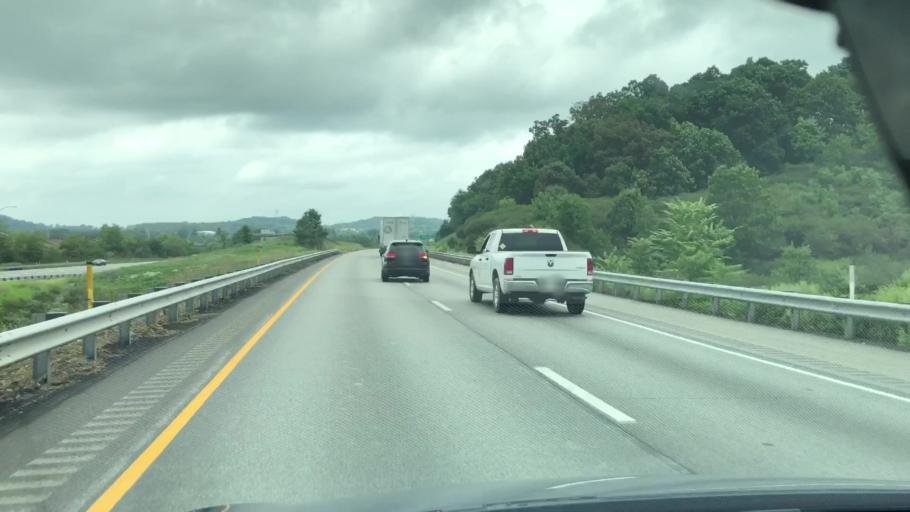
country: US
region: Pennsylvania
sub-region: Butler County
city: Cranberry Township
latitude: 40.6953
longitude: -80.0993
